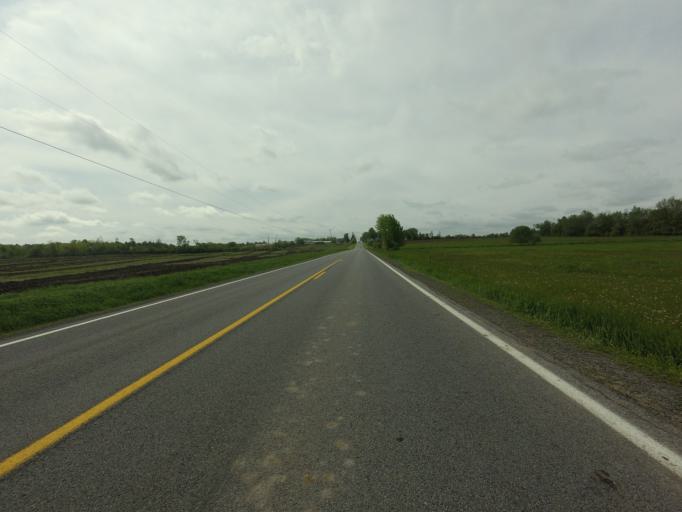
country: CA
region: Ontario
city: Cornwall
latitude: 44.7170
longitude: -74.6617
